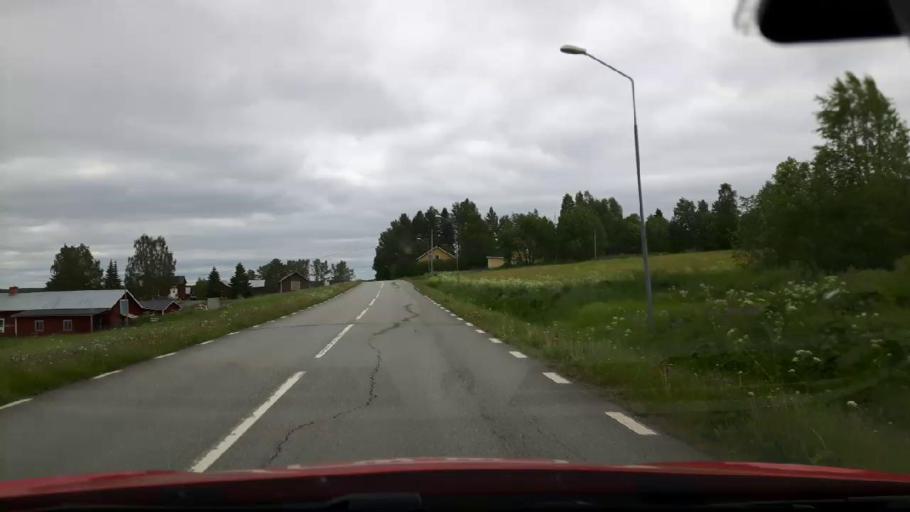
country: SE
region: Jaemtland
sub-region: Stroemsunds Kommun
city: Stroemsund
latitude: 63.5618
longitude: 15.3975
